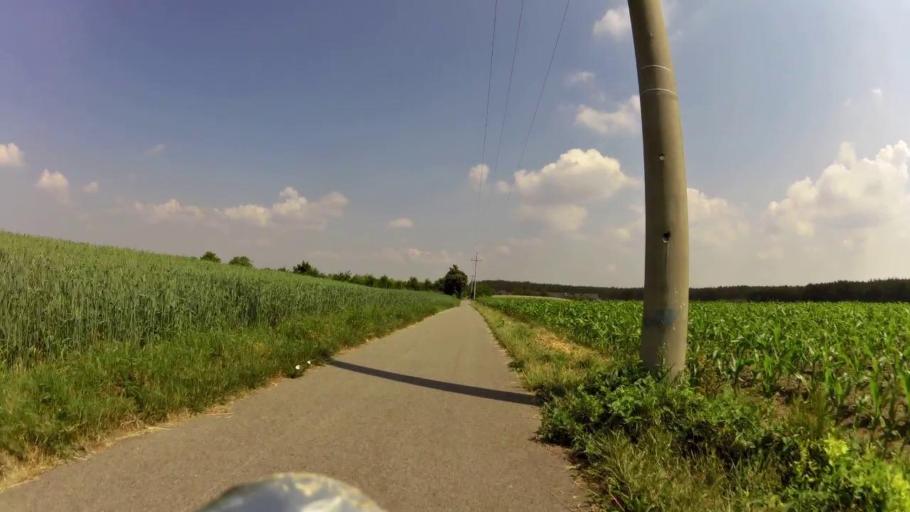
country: PL
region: Kujawsko-Pomorskie
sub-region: Powiat bydgoski
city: Koronowo
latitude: 53.2766
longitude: 17.9312
